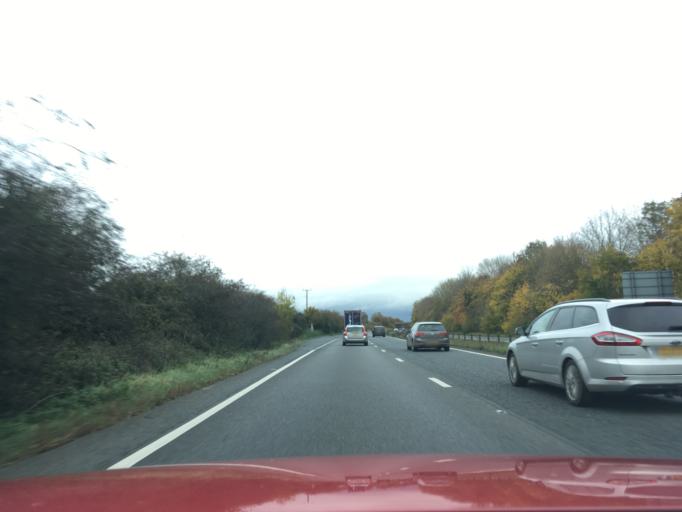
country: GB
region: England
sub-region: Somerset
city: Ilchester
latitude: 51.0093
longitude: -2.6884
